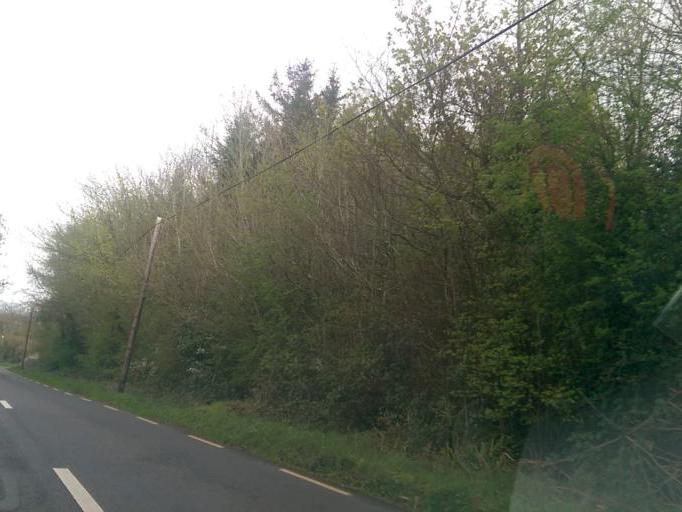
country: IE
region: Connaught
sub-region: County Galway
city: Ballinasloe
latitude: 53.4170
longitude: -8.3741
